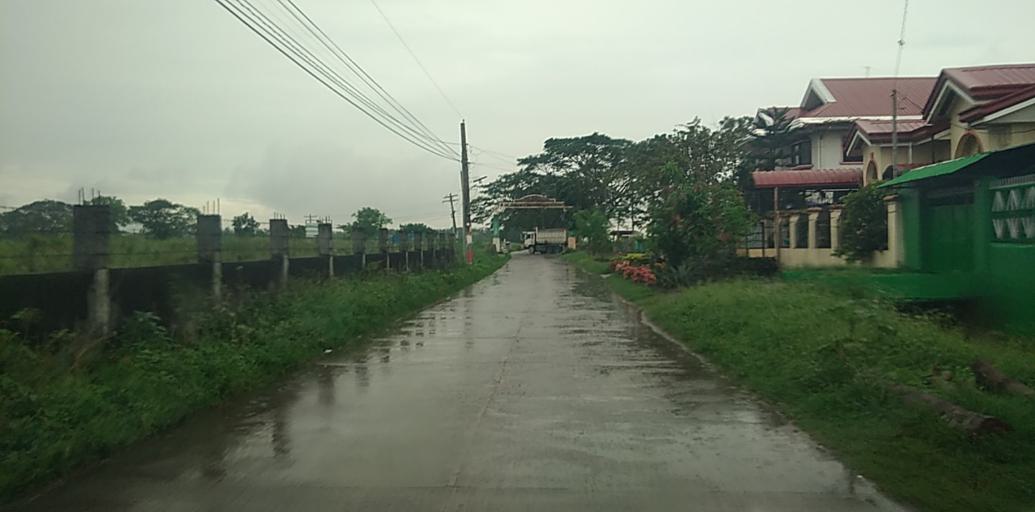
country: PH
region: Central Luzon
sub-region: Province of Pampanga
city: San Antonio
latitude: 15.1599
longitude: 120.6934
